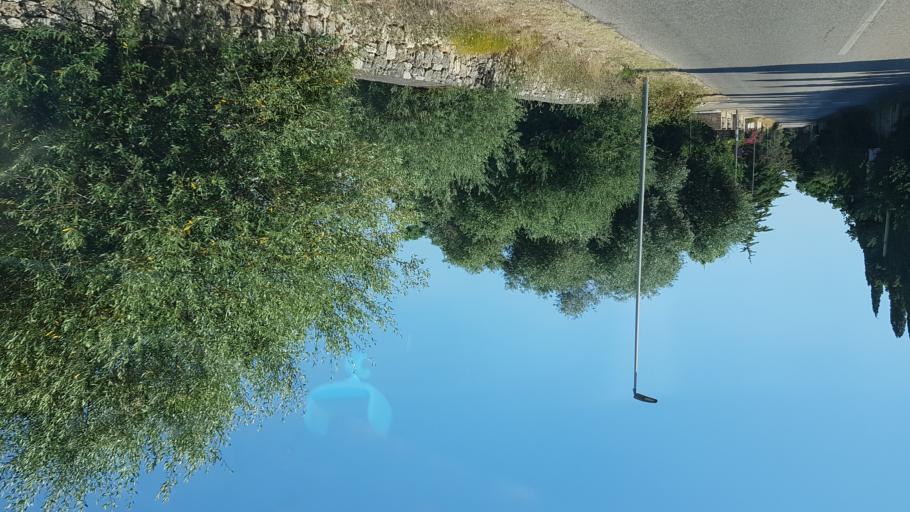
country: IT
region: Apulia
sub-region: Provincia di Lecce
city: Nardo
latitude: 40.1473
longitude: 17.9839
